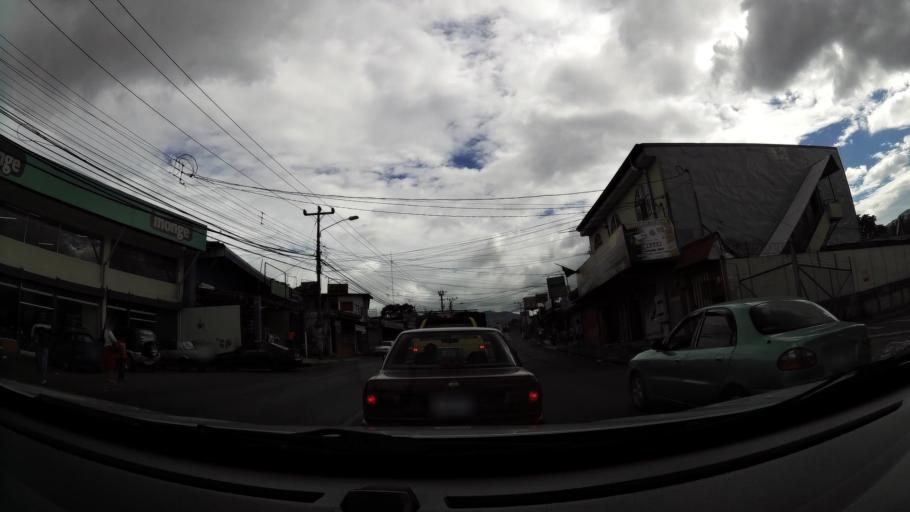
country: CR
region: San Jose
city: San Juan de Dios
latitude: 9.8931
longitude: -84.0821
